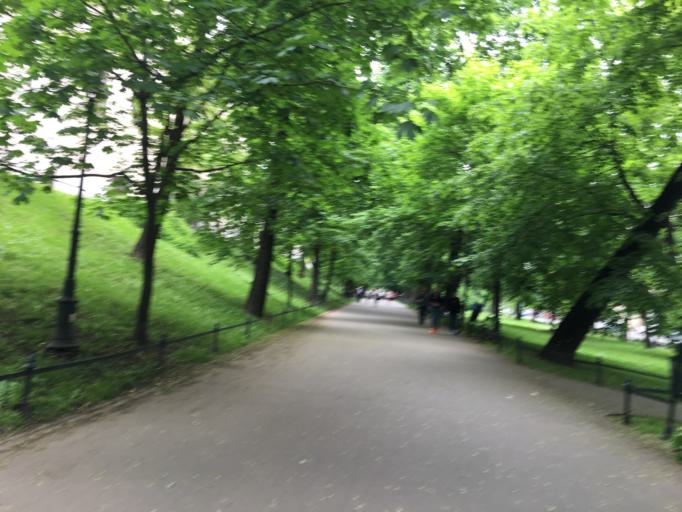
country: PL
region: Lesser Poland Voivodeship
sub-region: Krakow
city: Krakow
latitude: 50.0569
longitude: 19.9402
